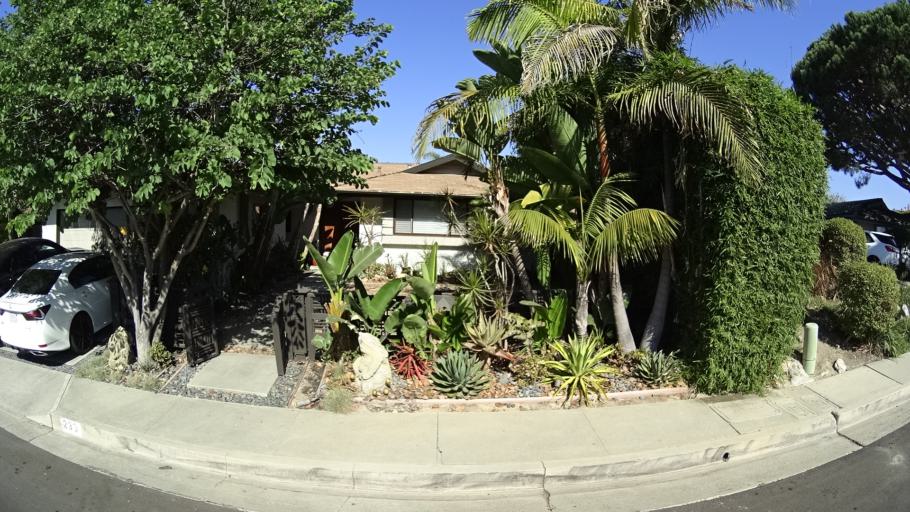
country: US
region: California
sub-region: Orange County
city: San Clemente
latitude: 33.4278
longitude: -117.6069
